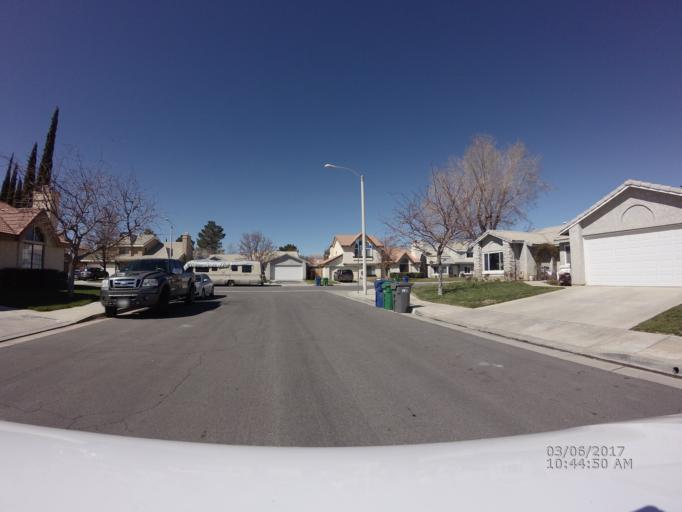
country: US
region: California
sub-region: Los Angeles County
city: Quartz Hill
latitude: 34.6548
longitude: -118.2218
